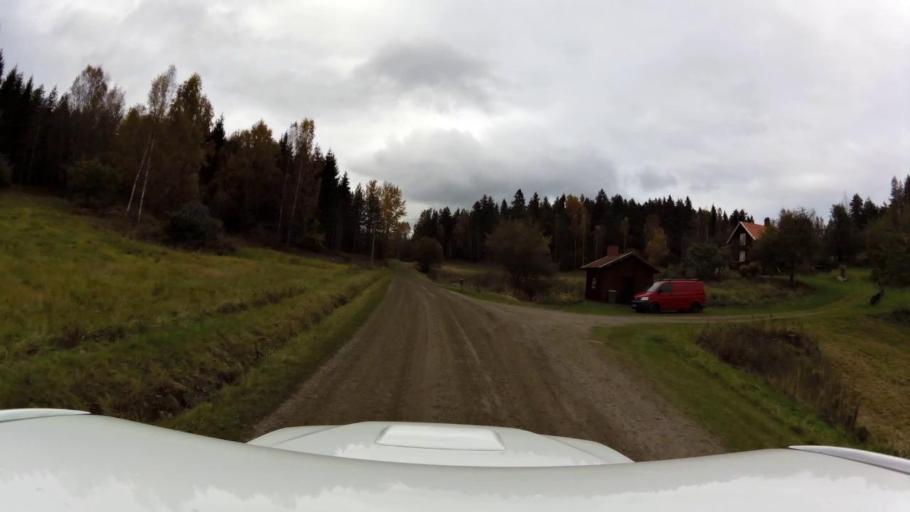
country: SE
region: OEstergoetland
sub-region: Linkopings Kommun
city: Ljungsbro
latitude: 58.5778
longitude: 15.4408
